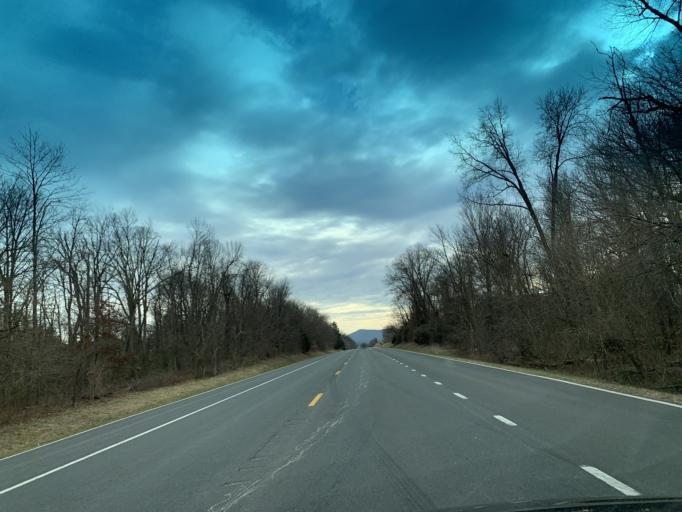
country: US
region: Maryland
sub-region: Washington County
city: Boonsboro
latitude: 39.4824
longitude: -77.6518
